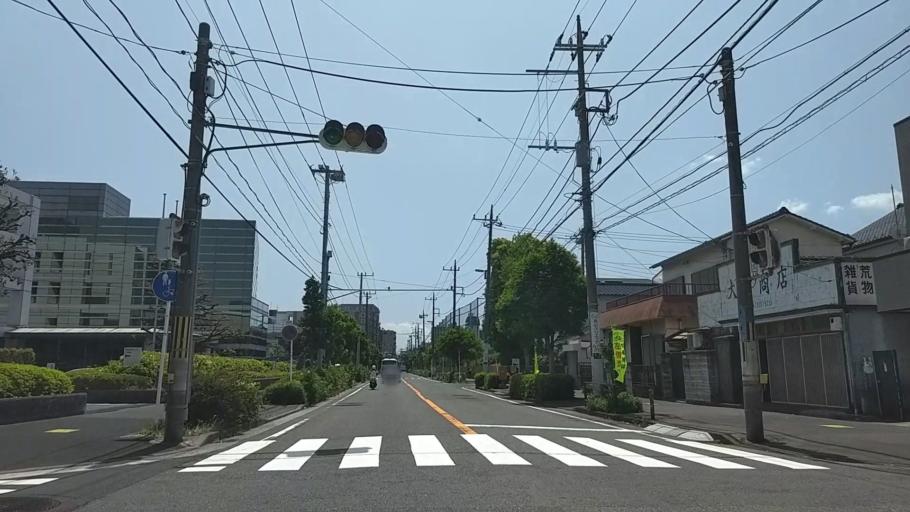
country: JP
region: Kanagawa
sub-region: Kawasaki-shi
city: Kawasaki
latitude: 35.5283
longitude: 139.7230
